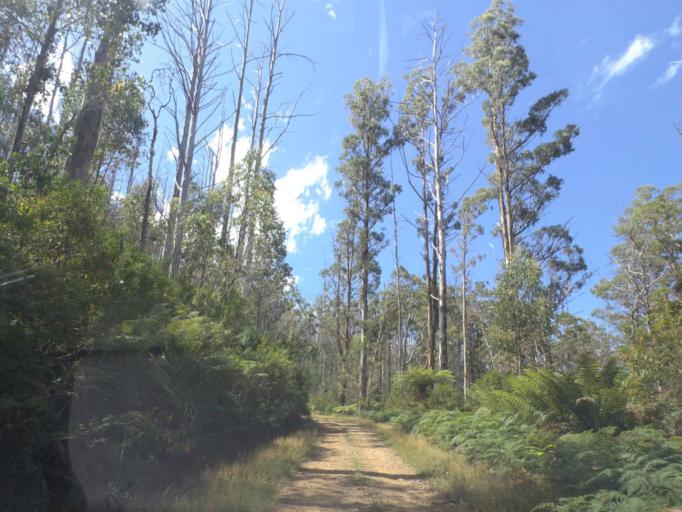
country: AU
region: Victoria
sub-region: Murrindindi
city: Alexandra
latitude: -37.4712
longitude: 145.8214
